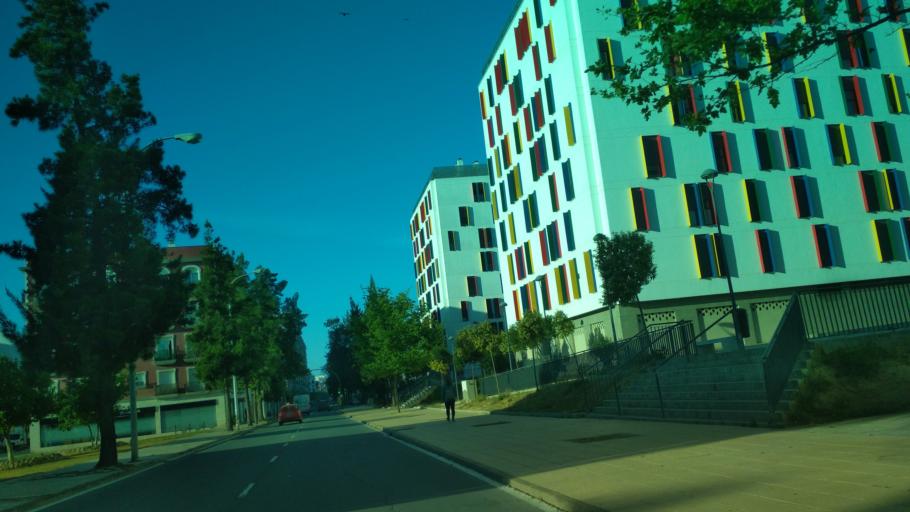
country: ES
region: Andalusia
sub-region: Provincia de Huelva
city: Huelva
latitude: 37.2743
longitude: -6.9498
